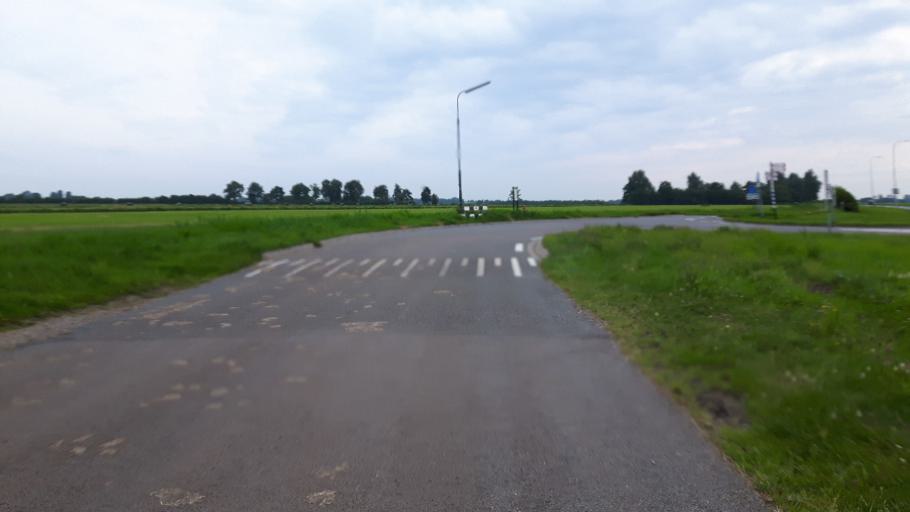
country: NL
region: Utrecht
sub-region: Stichtse Vecht
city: Breukelen
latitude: 52.1489
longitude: 4.9291
